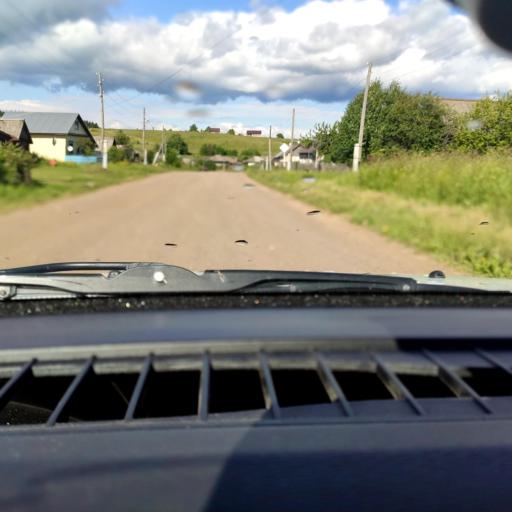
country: RU
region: Perm
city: Uinskoye
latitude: 57.1166
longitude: 56.5053
